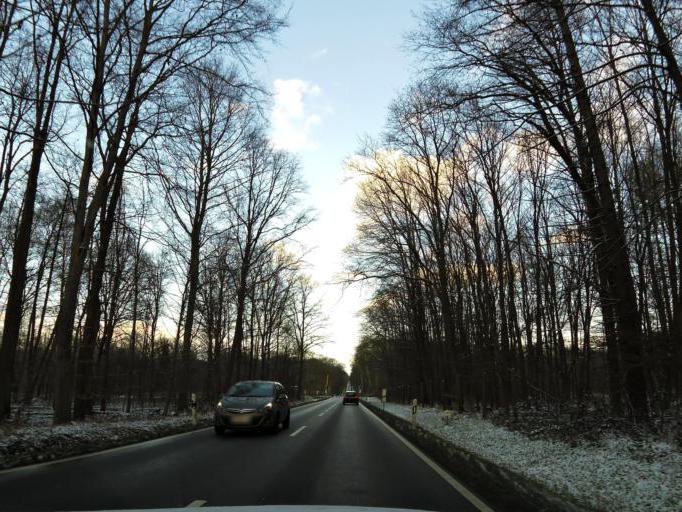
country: DE
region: Hesse
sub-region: Regierungsbezirk Darmstadt
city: Messel
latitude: 49.9168
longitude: 8.7153
